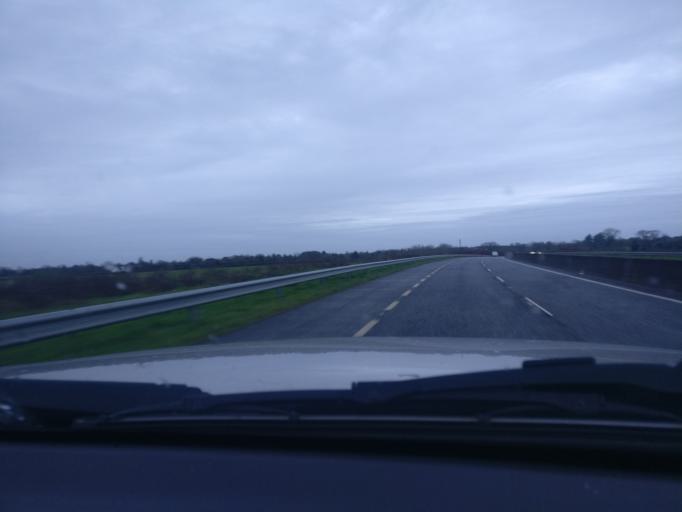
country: IE
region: Leinster
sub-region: An Mhi
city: Navan
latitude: 53.6470
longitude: -6.7197
